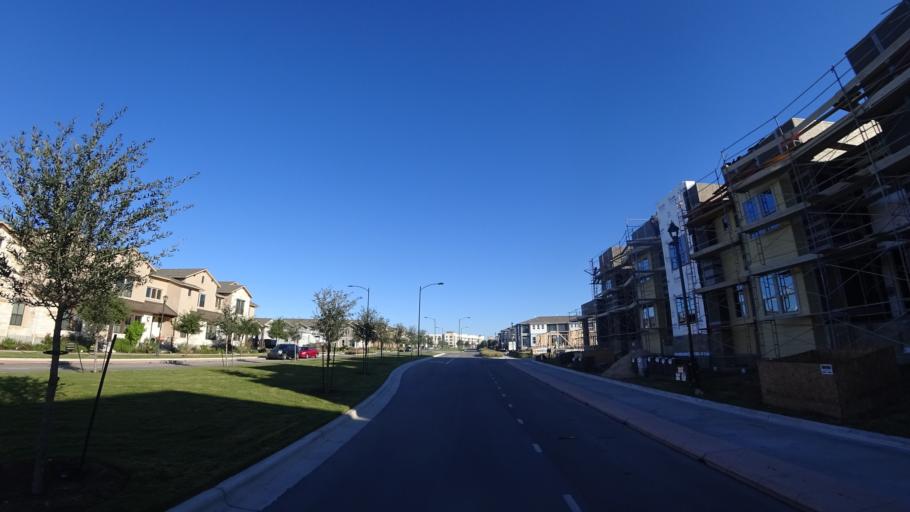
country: US
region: Texas
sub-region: Travis County
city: Austin
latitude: 30.2979
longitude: -97.7002
